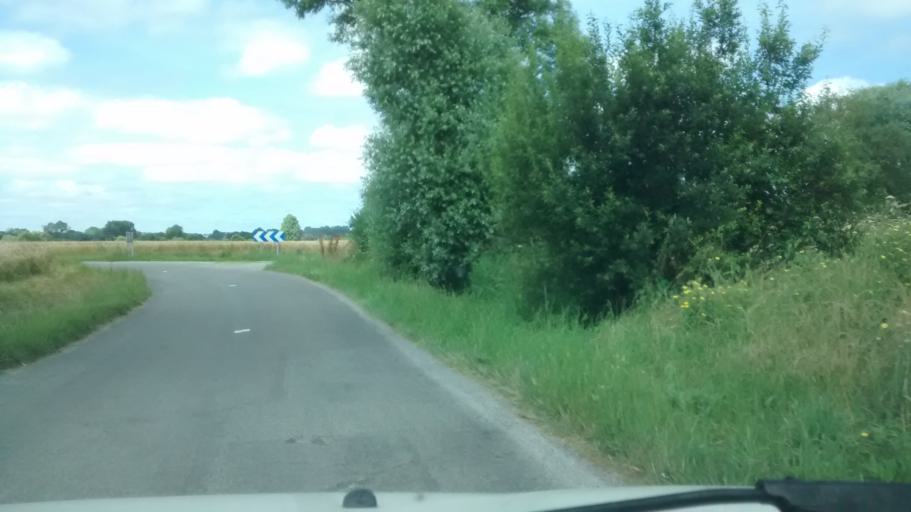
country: FR
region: Brittany
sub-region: Departement d'Ille-et-Vilaine
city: La Gouesniere
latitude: 48.6141
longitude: -1.8724
